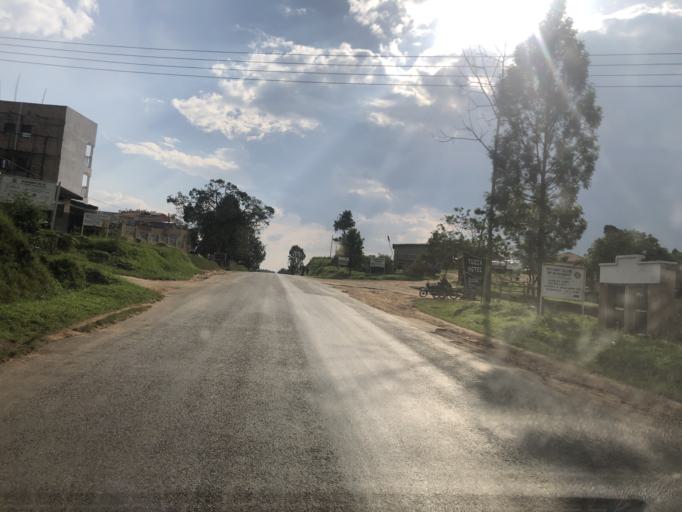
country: UG
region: Western Region
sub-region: Bushenyi District
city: Bushenyi
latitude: -0.5416
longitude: 30.1966
